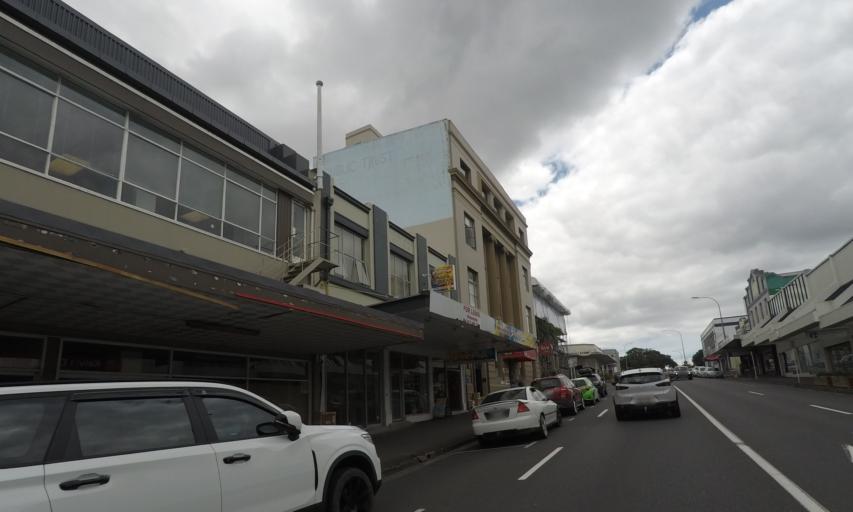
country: NZ
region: Northland
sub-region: Whangarei
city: Whangarei
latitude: -35.7243
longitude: 174.3197
